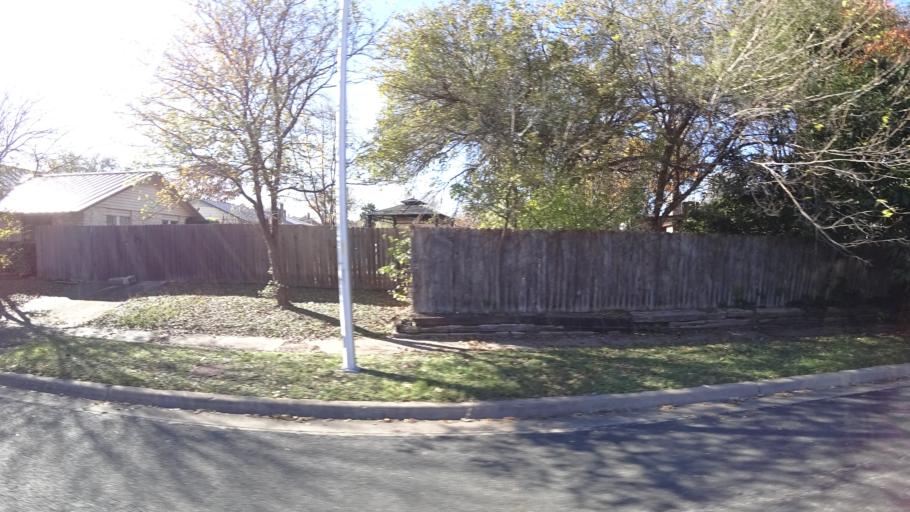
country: US
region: Texas
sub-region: Travis County
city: Wells Branch
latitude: 30.4179
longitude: -97.6953
